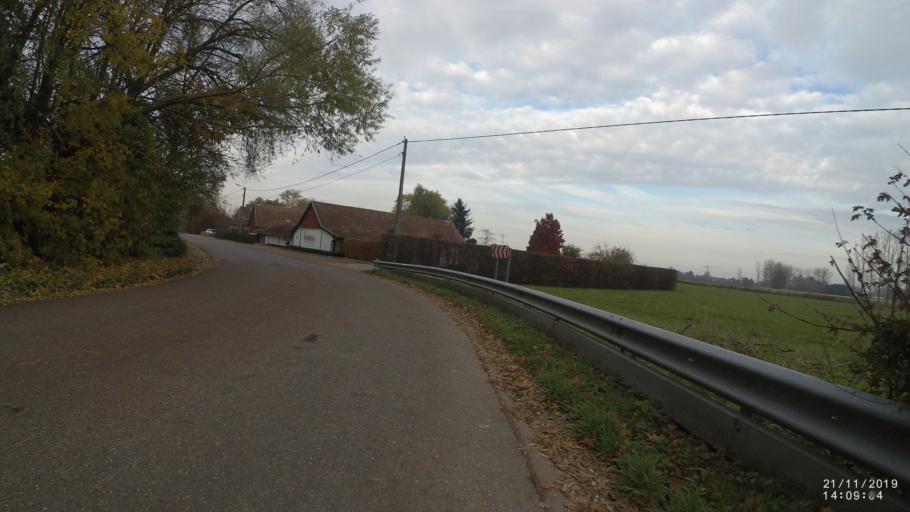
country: BE
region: Flanders
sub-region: Provincie Limburg
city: Alken
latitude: 50.8794
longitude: 5.2902
